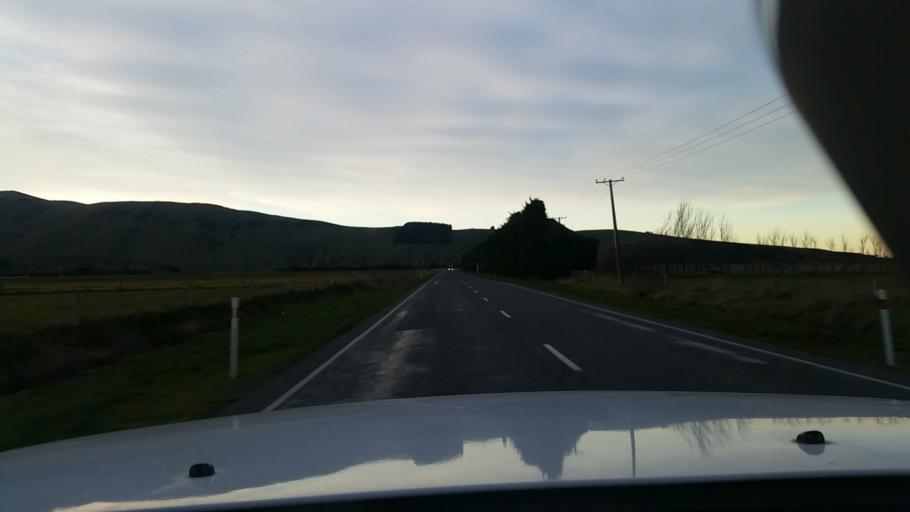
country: NZ
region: Canterbury
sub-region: Selwyn District
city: Lincoln
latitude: -43.7233
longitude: 172.5993
